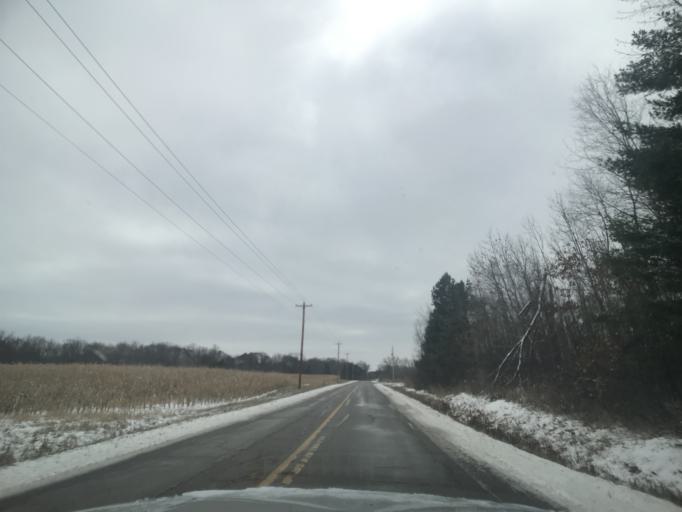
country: US
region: Wisconsin
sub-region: Brown County
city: Suamico
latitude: 44.7146
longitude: -88.0709
